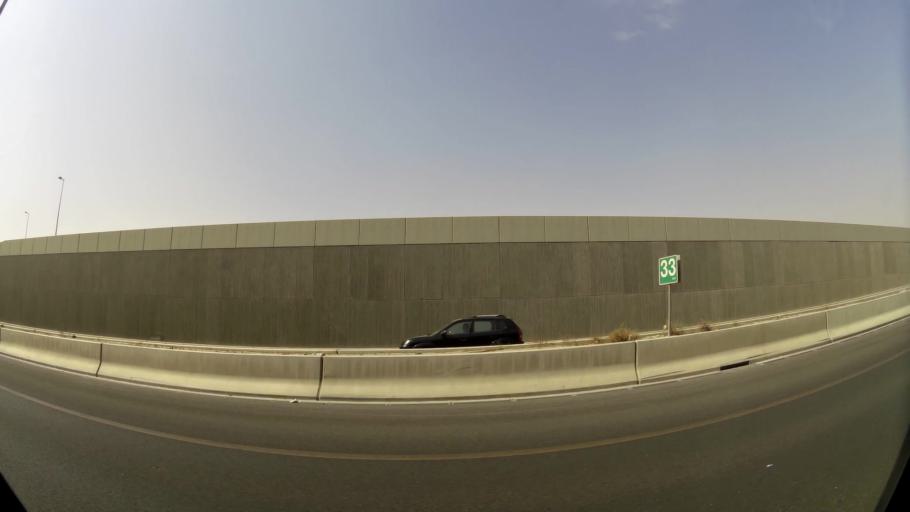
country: KW
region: Al Ahmadi
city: Al Manqaf
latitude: 29.1079
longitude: 48.1184
